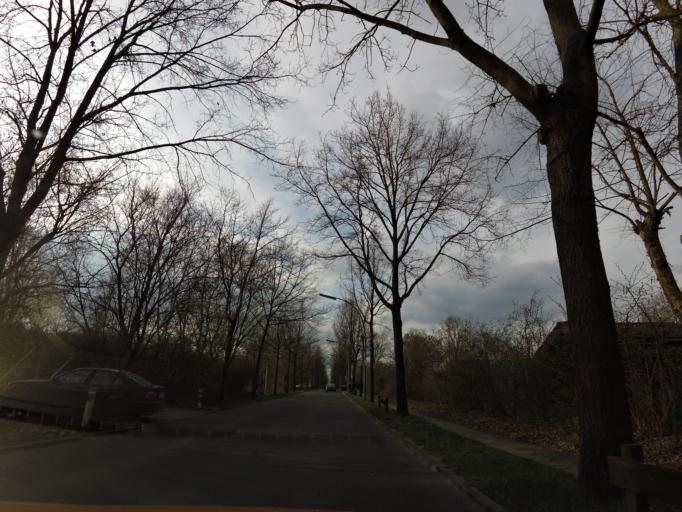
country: DE
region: Berlin
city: Lichterfelde
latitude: 52.4076
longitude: 13.3253
